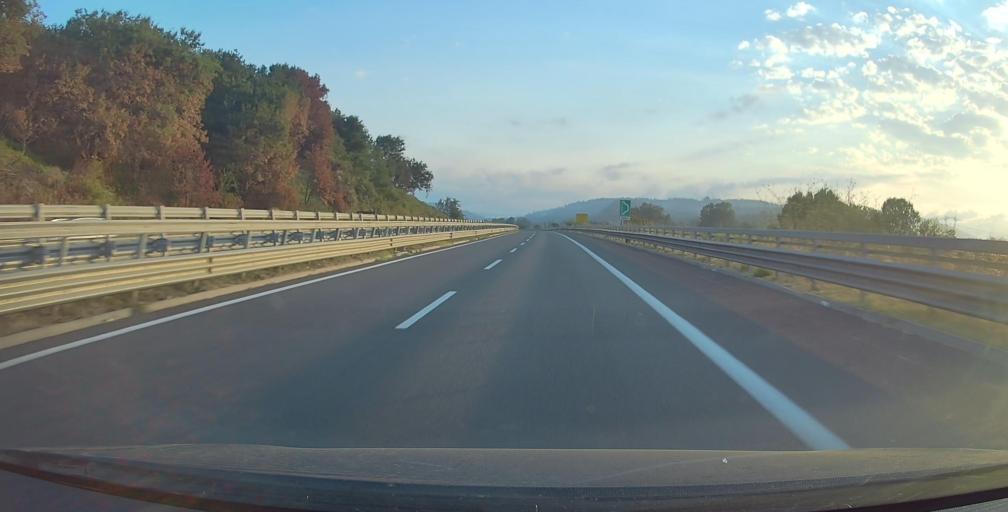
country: IT
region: Calabria
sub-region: Provincia di Reggio Calabria
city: Candidoni
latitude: 38.5164
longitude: 16.0506
